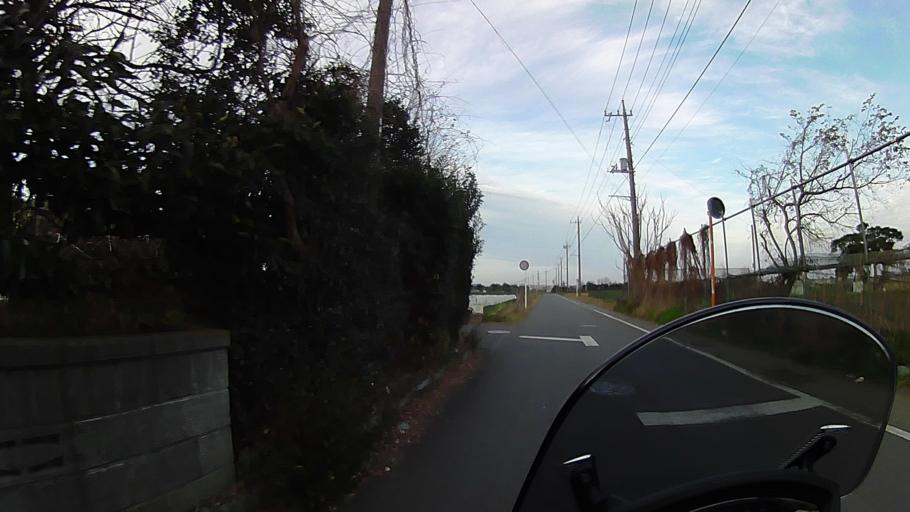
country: JP
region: Kanagawa
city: Minami-rinkan
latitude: 35.4286
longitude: 139.4211
